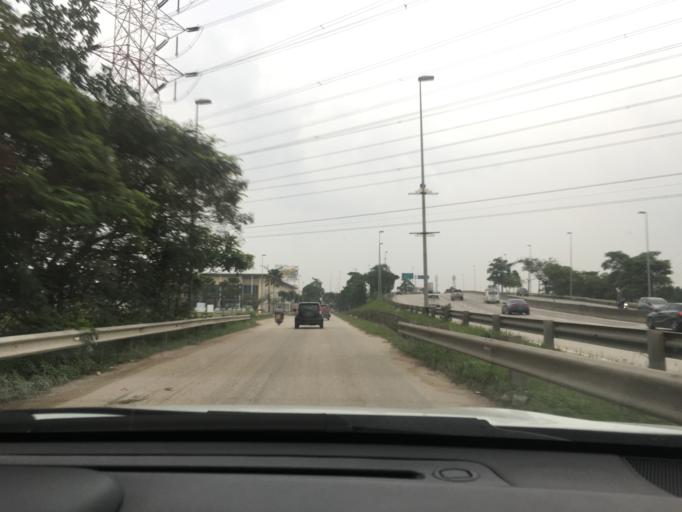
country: MY
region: Selangor
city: Klang
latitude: 3.1043
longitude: 101.4421
